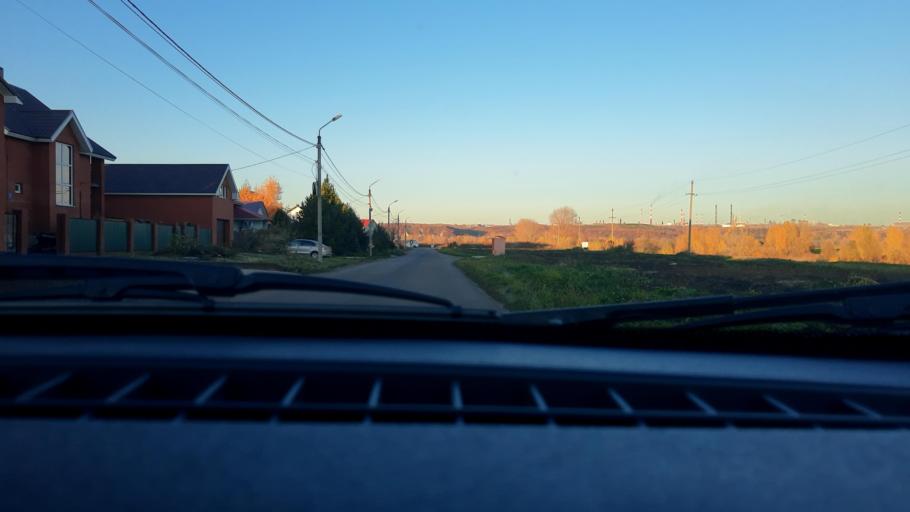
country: RU
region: Bashkortostan
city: Ufa
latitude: 54.8563
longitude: 56.0202
